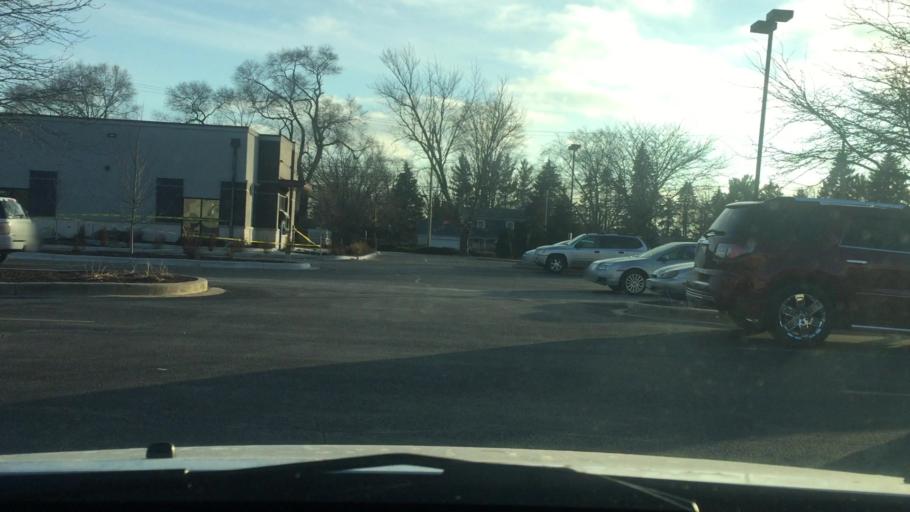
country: US
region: Wisconsin
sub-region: Waukesha County
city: Waukesha
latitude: 42.9892
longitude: -88.2445
